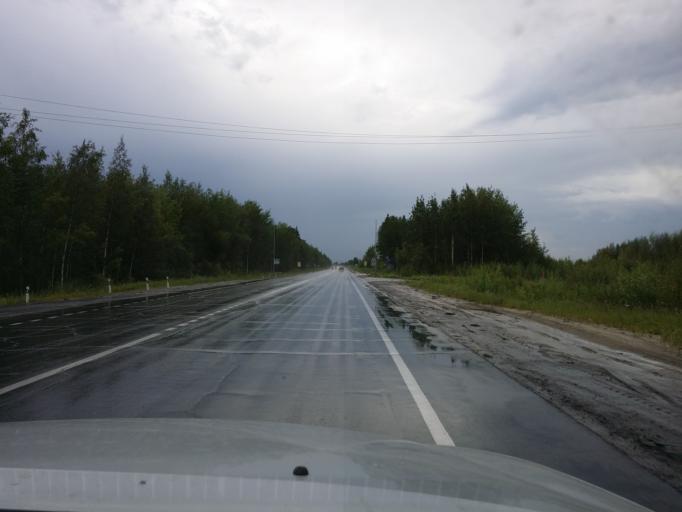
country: RU
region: Khanty-Mansiyskiy Avtonomnyy Okrug
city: Megion
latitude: 61.0642
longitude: 76.2675
